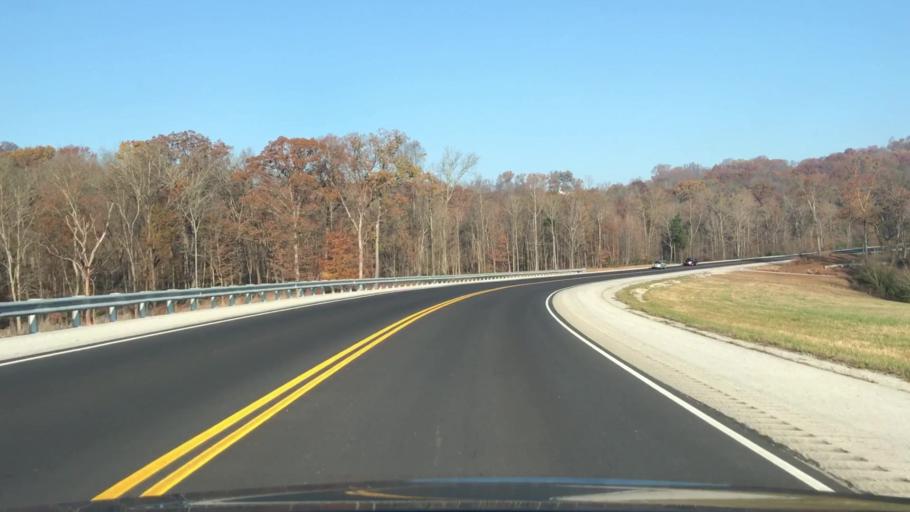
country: US
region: Kentucky
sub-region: Edmonson County
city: Brownsville
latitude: 37.0919
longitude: -86.2328
